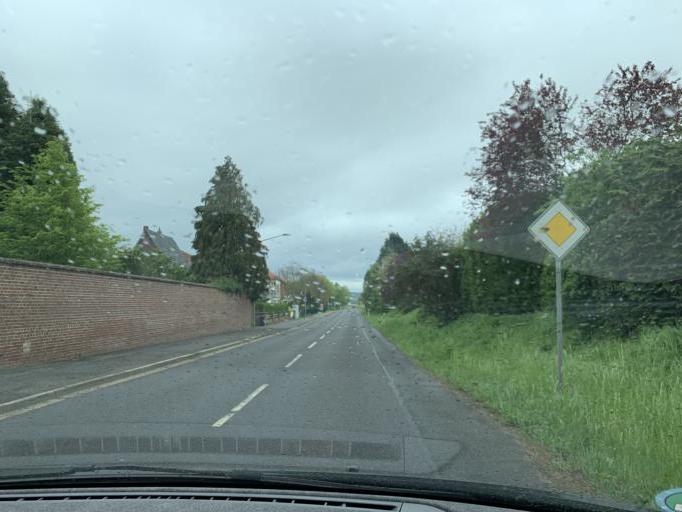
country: DE
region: North Rhine-Westphalia
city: Zulpich
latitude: 50.6830
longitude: 6.6436
